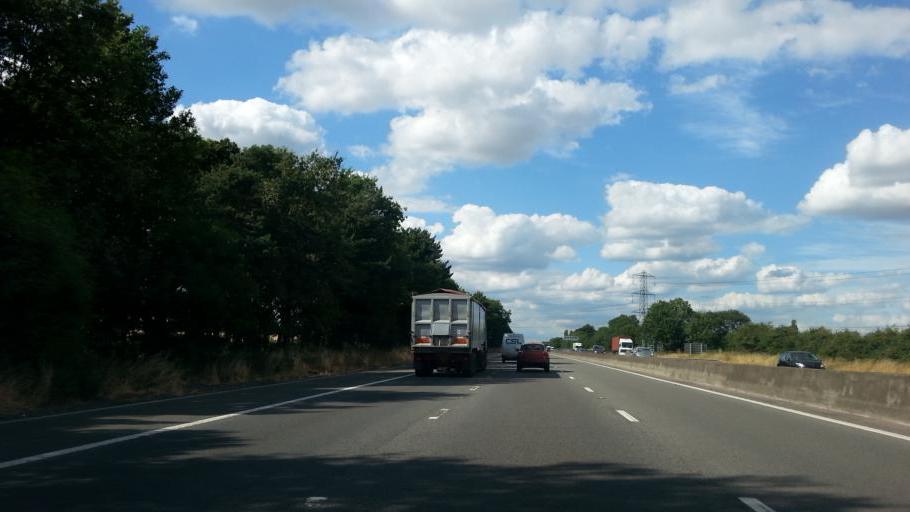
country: GB
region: England
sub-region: Leicestershire
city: Lutterworth
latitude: 52.4691
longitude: -1.1926
